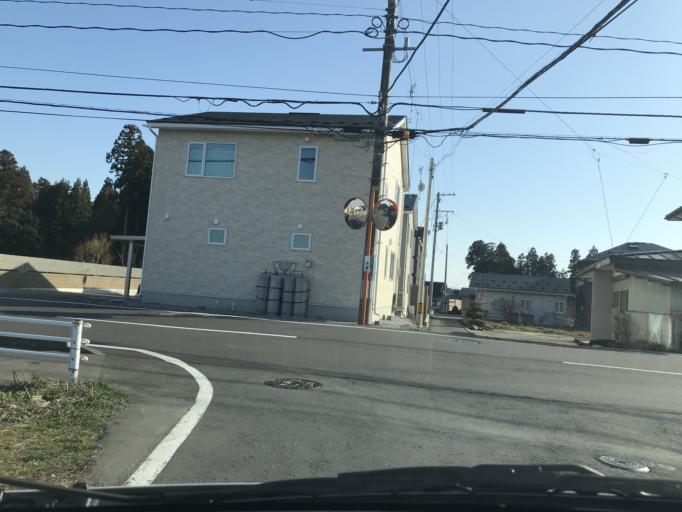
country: JP
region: Iwate
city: Kitakami
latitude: 39.2928
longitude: 141.0882
